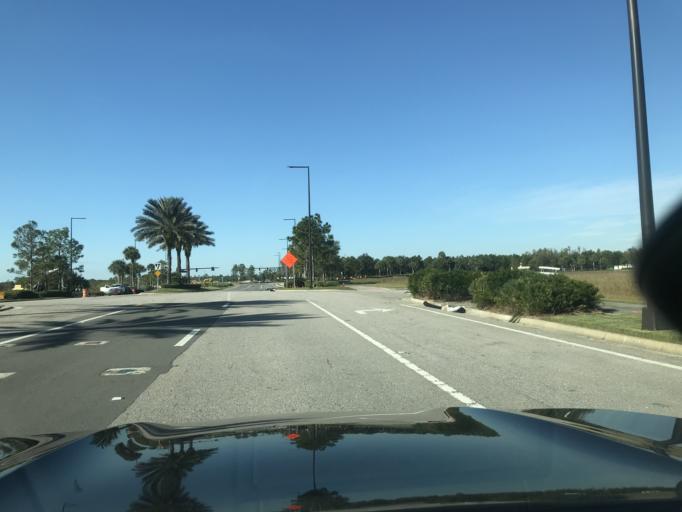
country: US
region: Florida
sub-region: Polk County
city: Citrus Ridge
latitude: 28.3782
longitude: -81.6172
